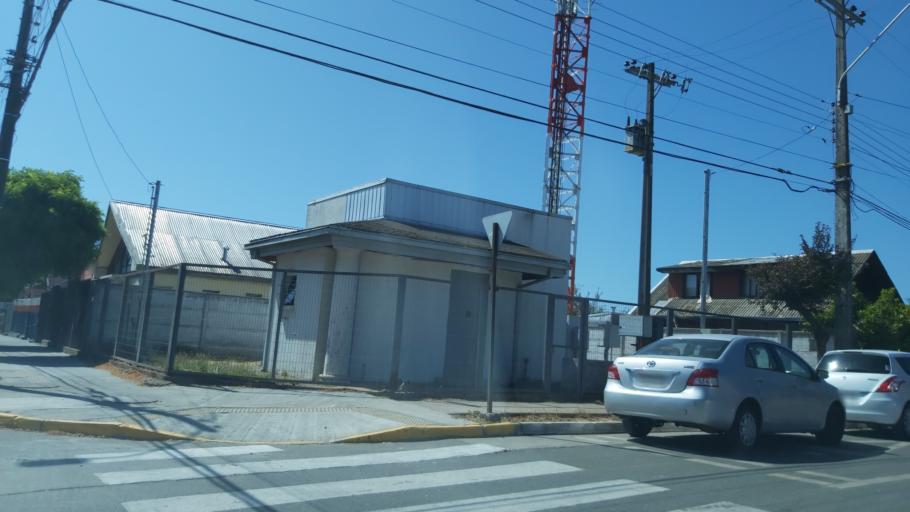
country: CL
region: Biobio
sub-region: Provincia de Concepcion
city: Lota
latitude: -37.1741
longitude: -72.9378
